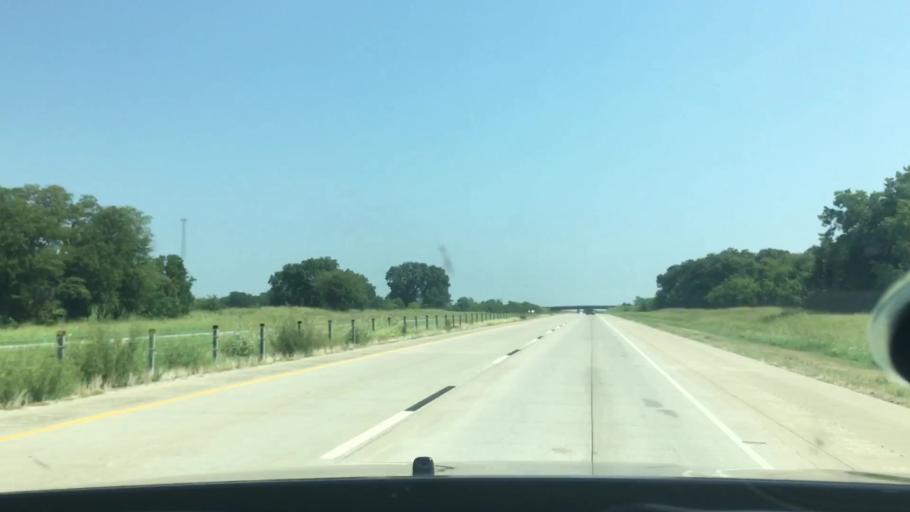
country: US
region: Oklahoma
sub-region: Bryan County
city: Durant
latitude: 34.0708
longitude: -96.3429
